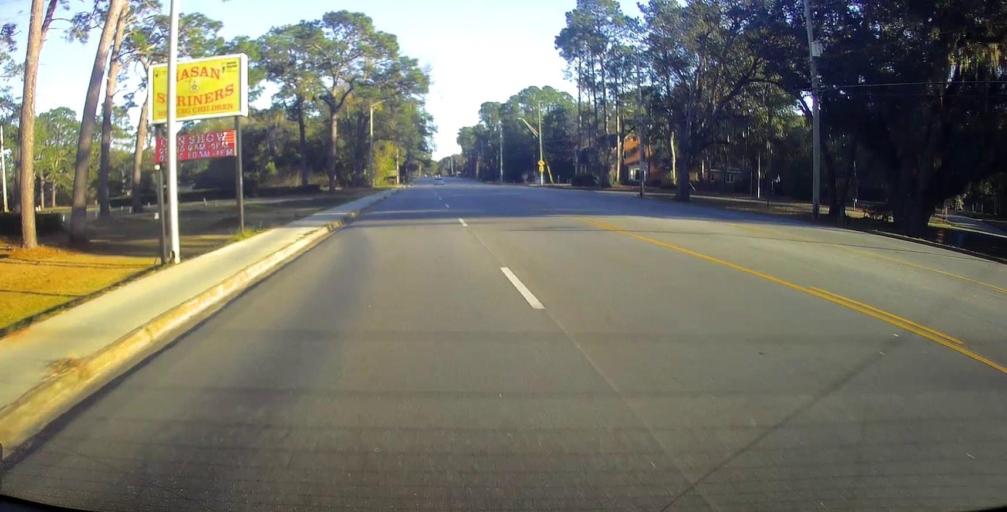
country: US
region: Georgia
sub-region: Dougherty County
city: Albany
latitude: 31.6017
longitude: -84.1677
